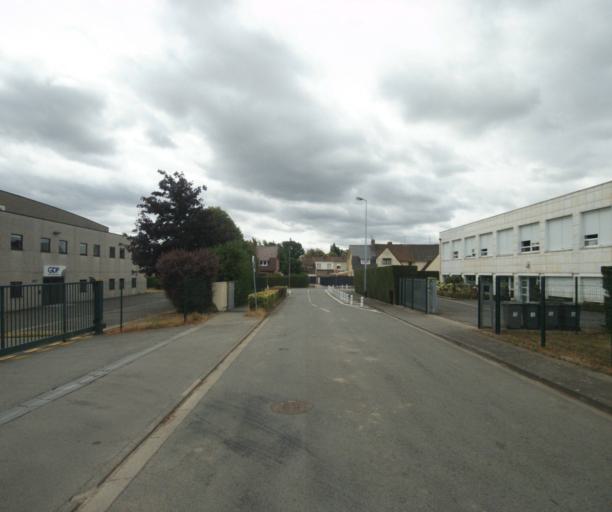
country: FR
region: Nord-Pas-de-Calais
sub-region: Departement du Nord
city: Linselles
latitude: 50.7479
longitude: 3.0883
